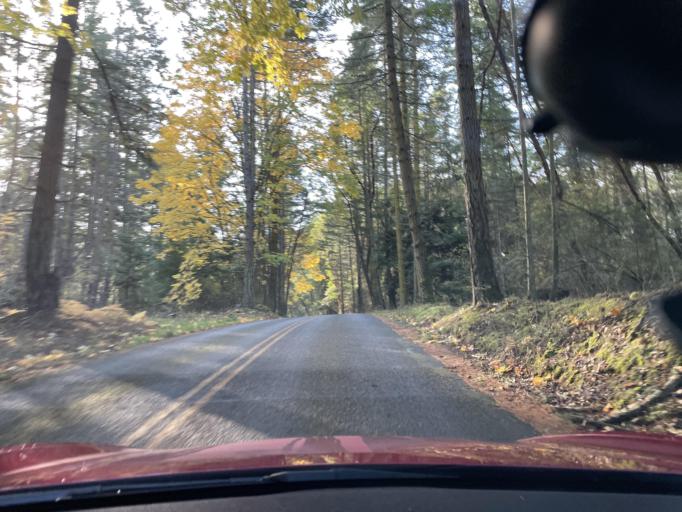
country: US
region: Washington
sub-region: San Juan County
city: Friday Harbor
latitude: 48.5216
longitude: -123.1445
